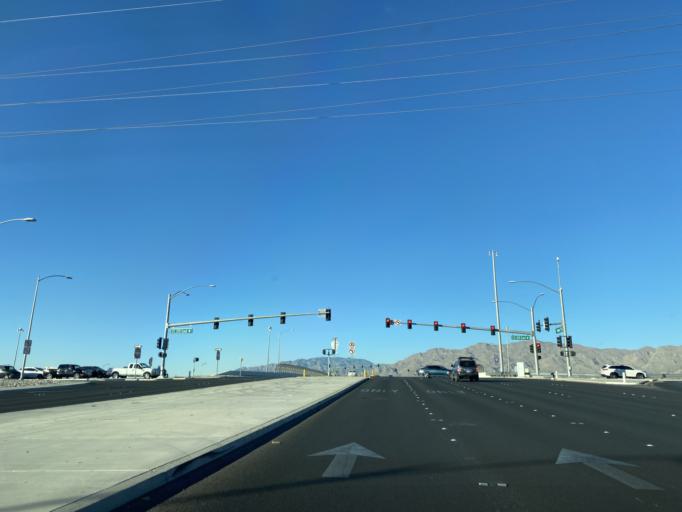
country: US
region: Nevada
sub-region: Clark County
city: North Las Vegas
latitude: 36.2738
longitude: -115.2249
